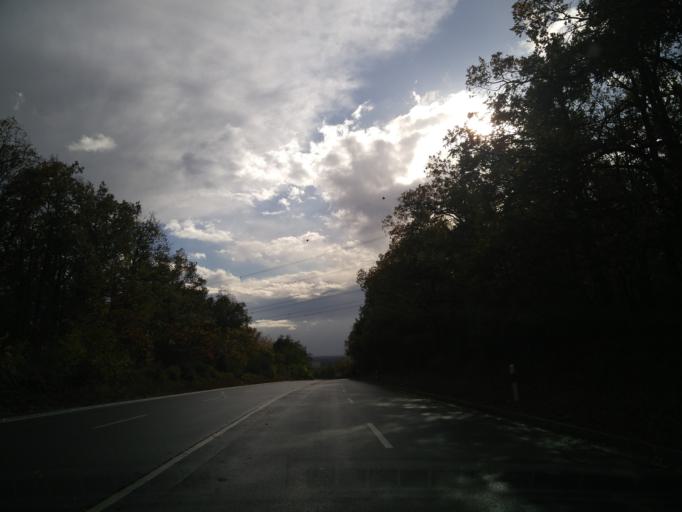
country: HU
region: Pest
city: Kerepes
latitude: 47.5819
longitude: 19.2928
